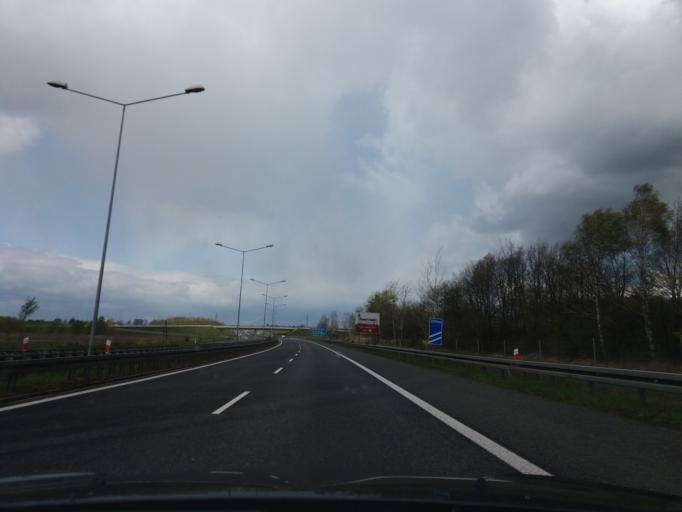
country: PL
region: Silesian Voivodeship
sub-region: Powiat gliwicki
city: Rudziniec
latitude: 50.3897
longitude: 18.4536
